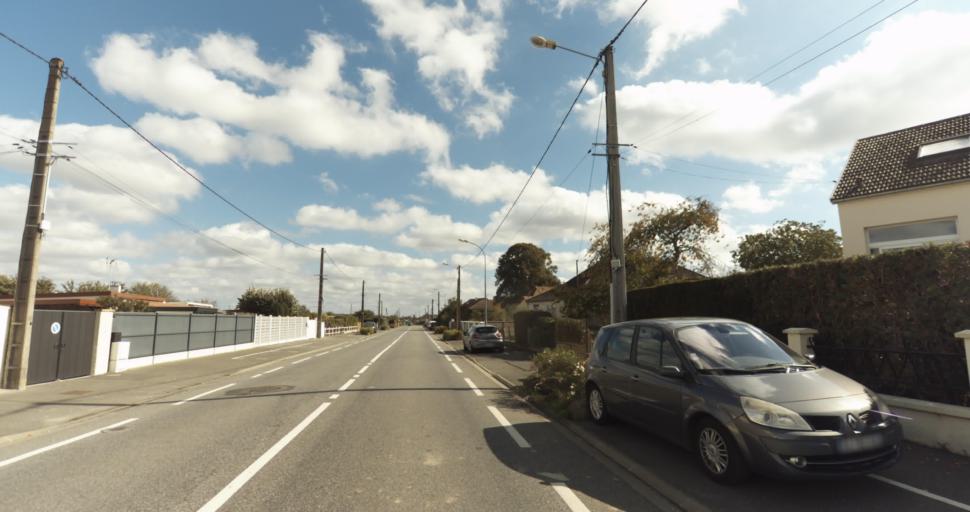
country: FR
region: Centre
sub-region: Departement d'Eure-et-Loir
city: Garnay
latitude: 48.7291
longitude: 1.3277
